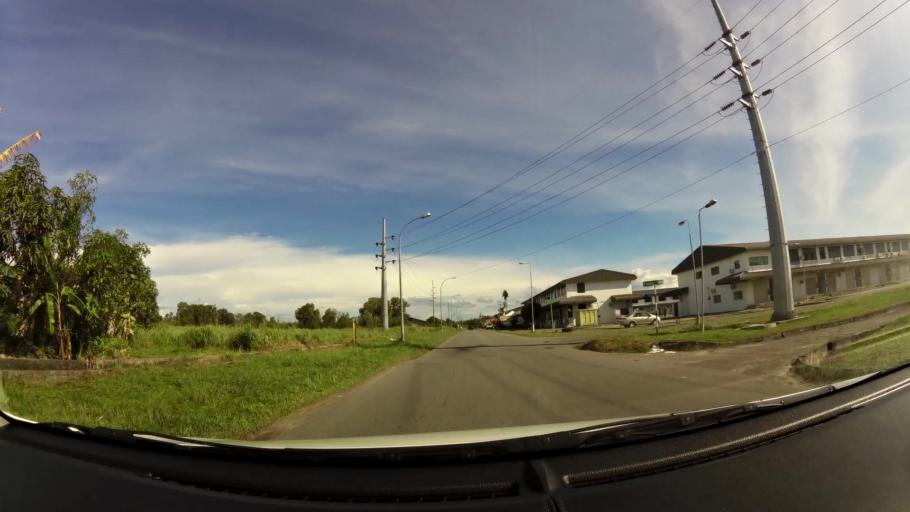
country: BN
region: Belait
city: Kuala Belait
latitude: 4.5765
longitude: 114.2087
